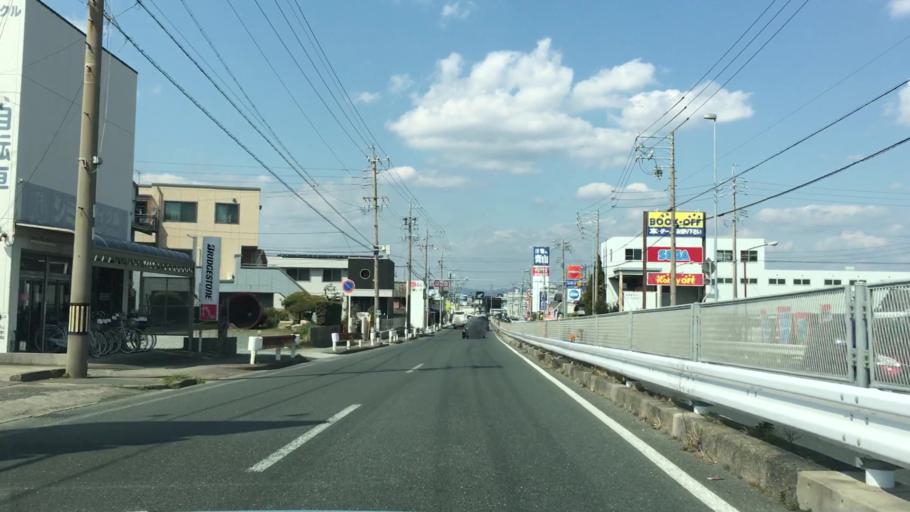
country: JP
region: Aichi
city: Toyohashi
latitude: 34.7488
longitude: 137.4134
